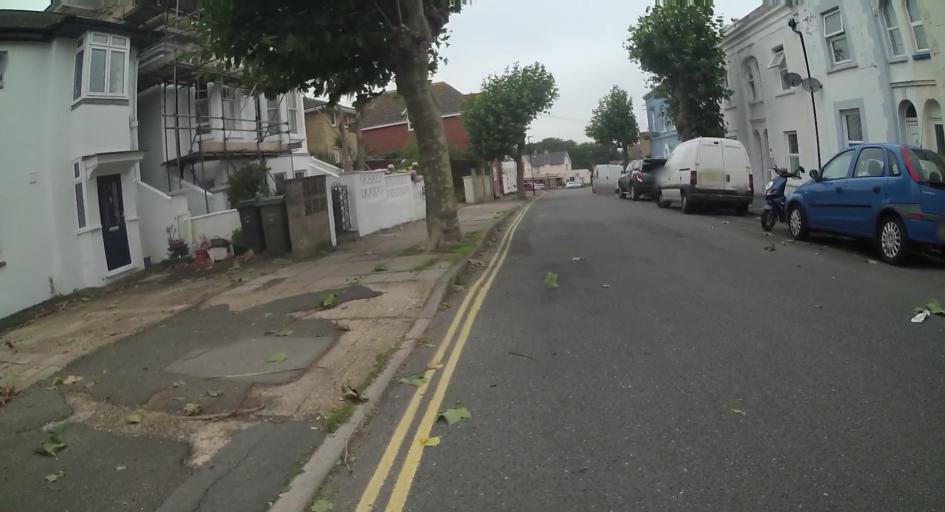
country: GB
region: England
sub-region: Isle of Wight
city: Sandown
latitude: 50.6568
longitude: -1.1603
